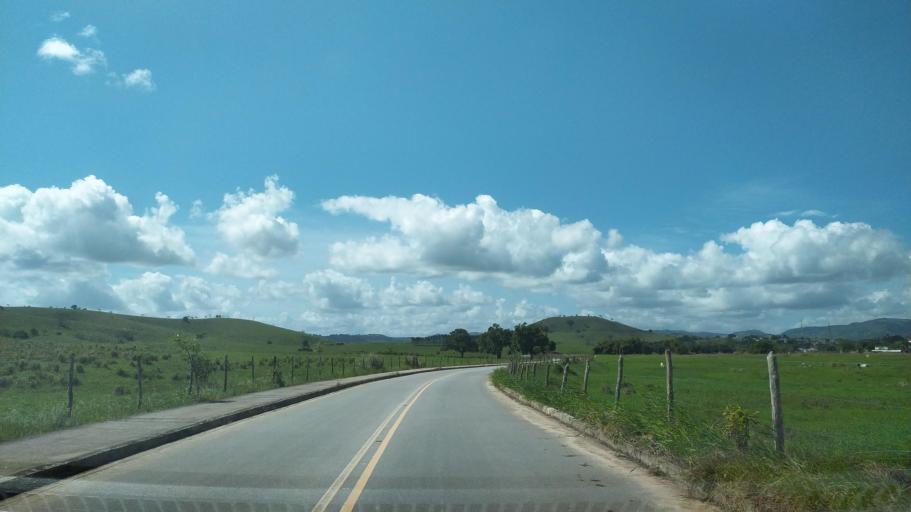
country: BR
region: Alagoas
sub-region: Uniao Dos Palmares
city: Uniao dos Palmares
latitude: -9.1621
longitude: -36.0480
